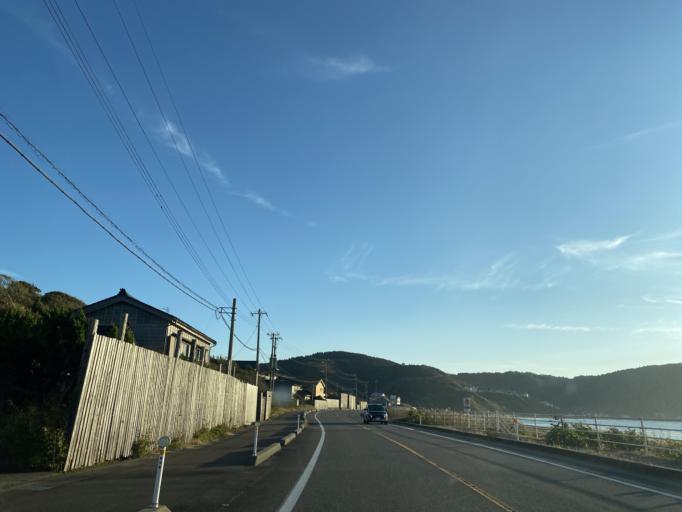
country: JP
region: Niigata
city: Kashiwazaki
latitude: 37.4941
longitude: 138.6344
